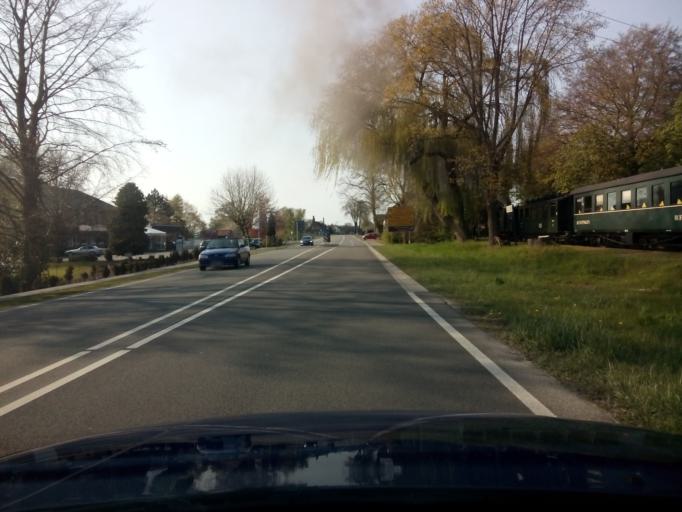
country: DE
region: Lower Saxony
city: Bruchhausen-Vilsen
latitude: 52.8013
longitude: 8.9749
